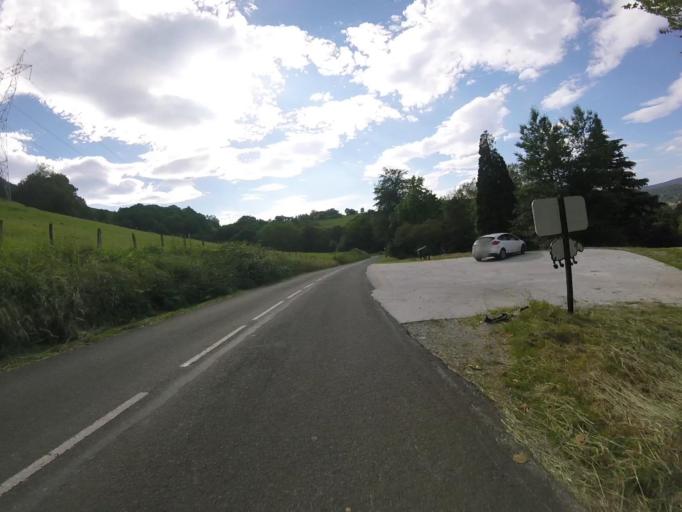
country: ES
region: Basque Country
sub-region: Provincia de Guipuzcoa
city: Errenteria
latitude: 43.2792
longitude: -1.8553
